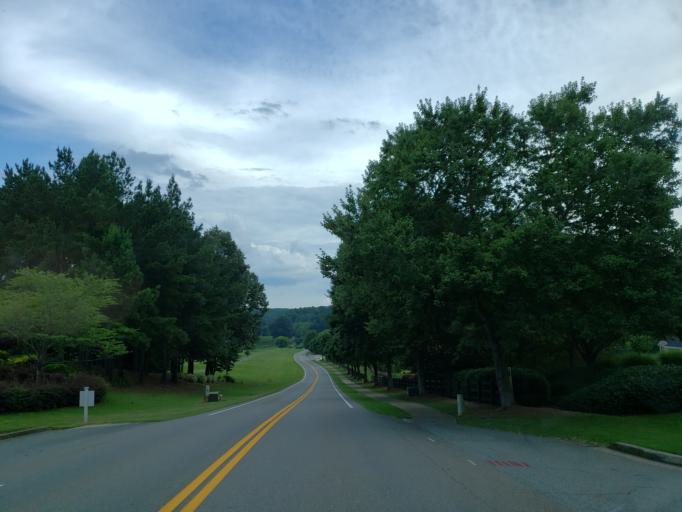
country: US
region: Georgia
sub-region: Cherokee County
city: Ball Ground
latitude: 34.2326
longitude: -84.3553
